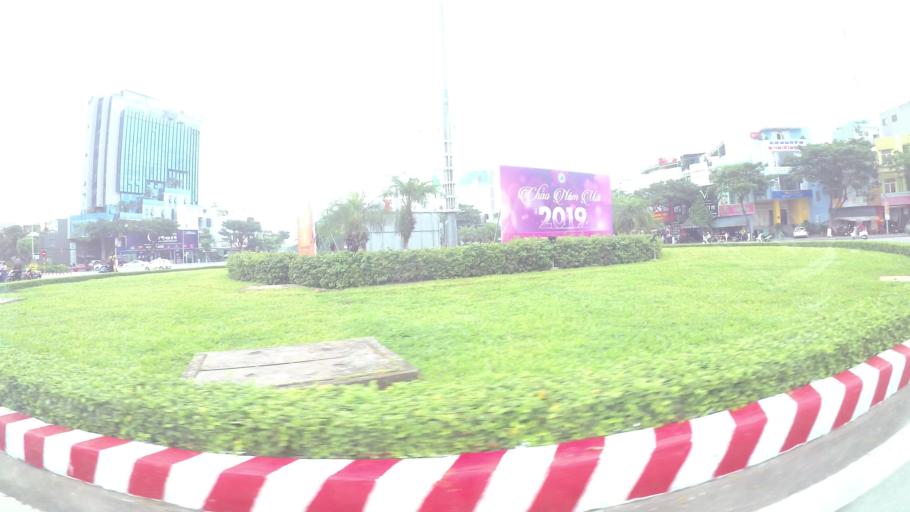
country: VN
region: Da Nang
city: Da Nang
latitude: 16.0504
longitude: 108.2092
